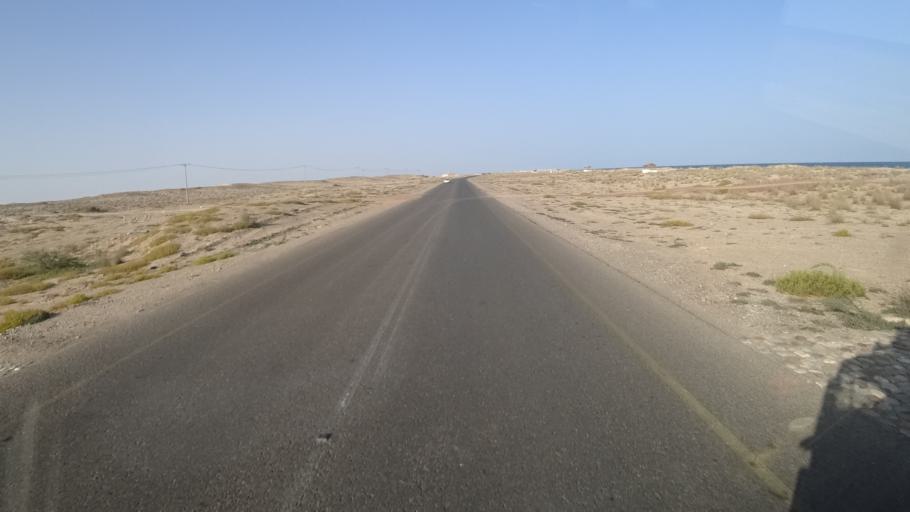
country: OM
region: Ash Sharqiyah
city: Sur
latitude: 22.1427
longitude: 59.7316
